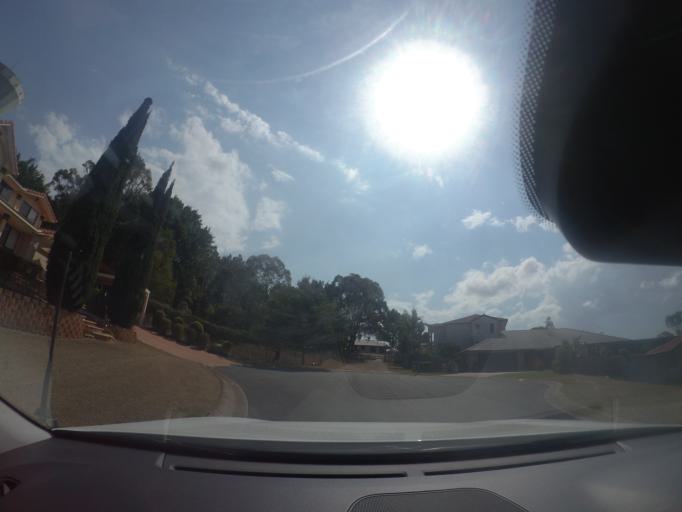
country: AU
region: Queensland
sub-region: Logan
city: Springwood
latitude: -27.6111
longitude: 153.1086
